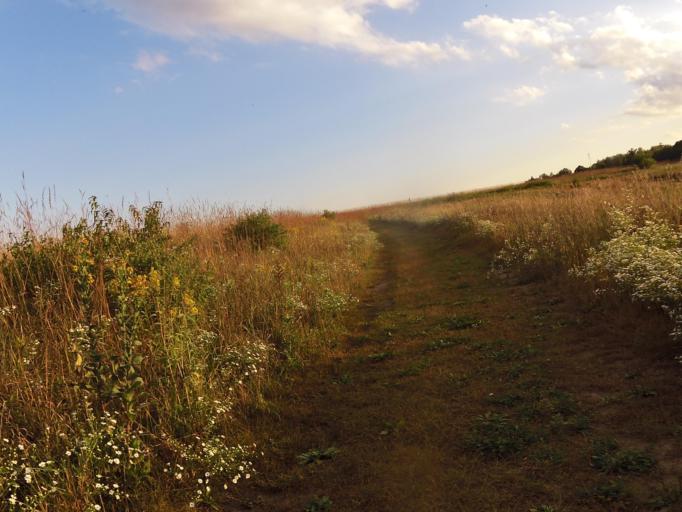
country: US
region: Minnesota
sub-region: Washington County
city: Lake Saint Croix Beach
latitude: 44.9353
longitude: -92.7897
